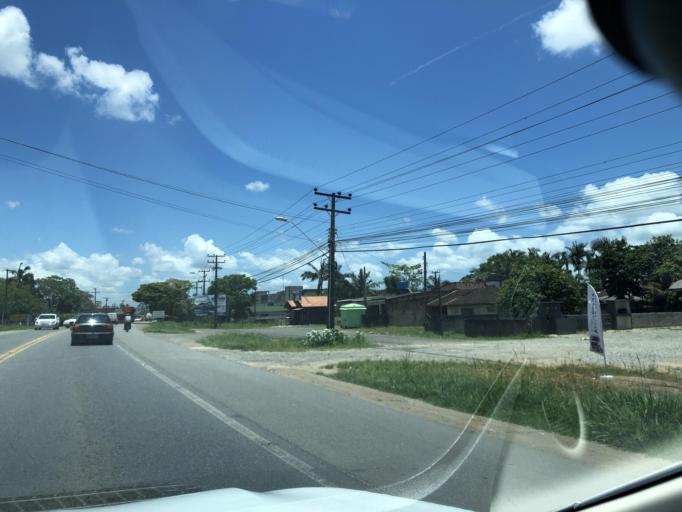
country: BR
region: Santa Catarina
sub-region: Joinville
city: Joinville
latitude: -26.4048
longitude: -48.7458
